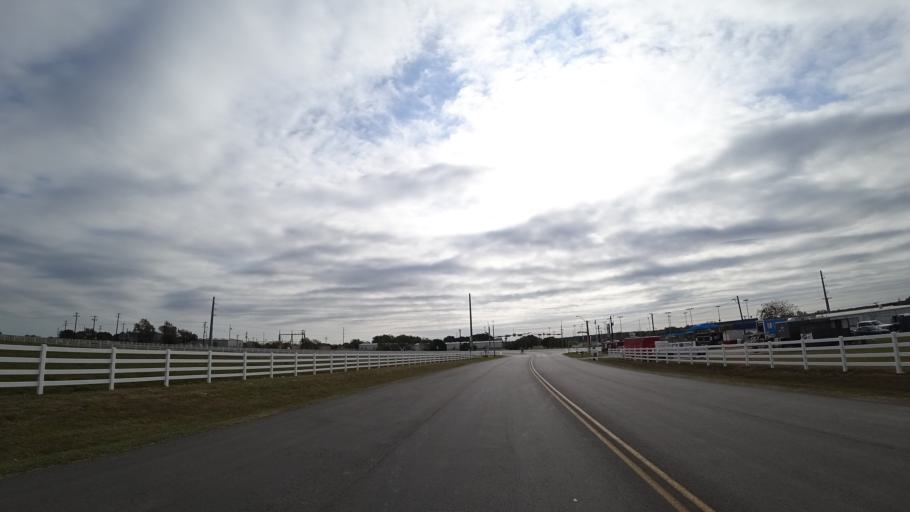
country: US
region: Texas
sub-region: Travis County
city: Manchaca
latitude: 30.1354
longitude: -97.8540
